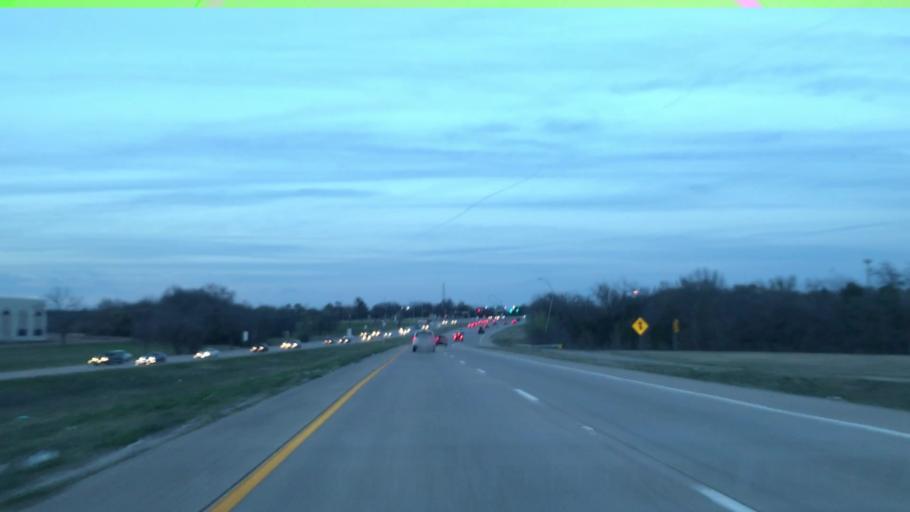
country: US
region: Texas
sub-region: Dallas County
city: Coppell
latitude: 32.9913
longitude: -97.0071
